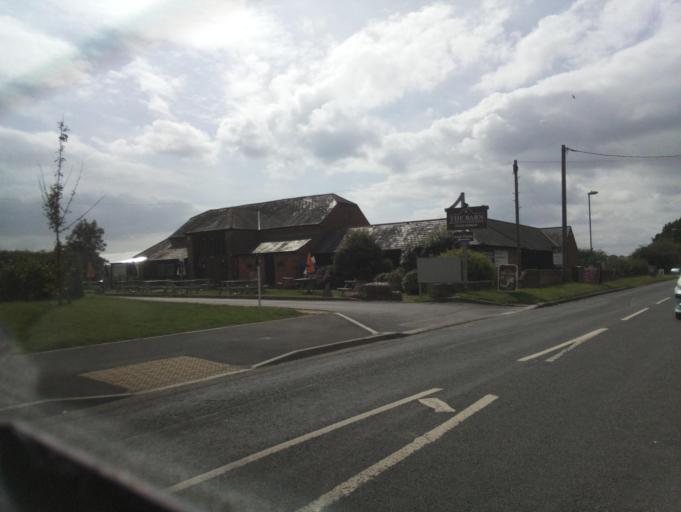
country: GB
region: England
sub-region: Hampshire
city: New Milton
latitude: 50.7516
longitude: -1.6688
